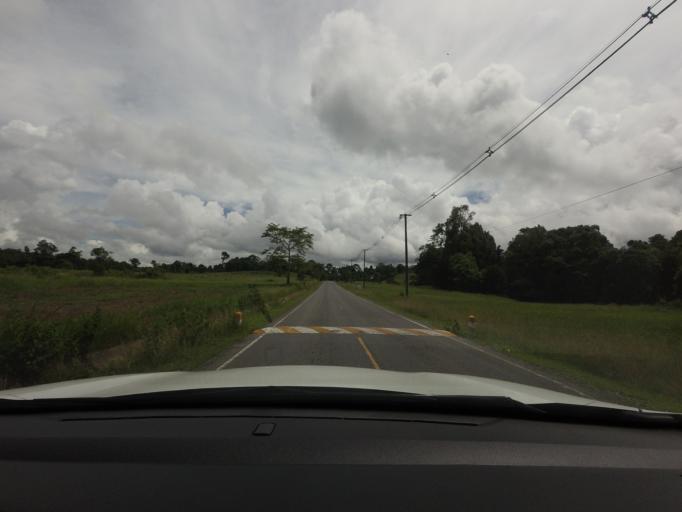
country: TH
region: Nakhon Nayok
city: Nakhon Nayok
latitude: 14.4171
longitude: 101.3713
